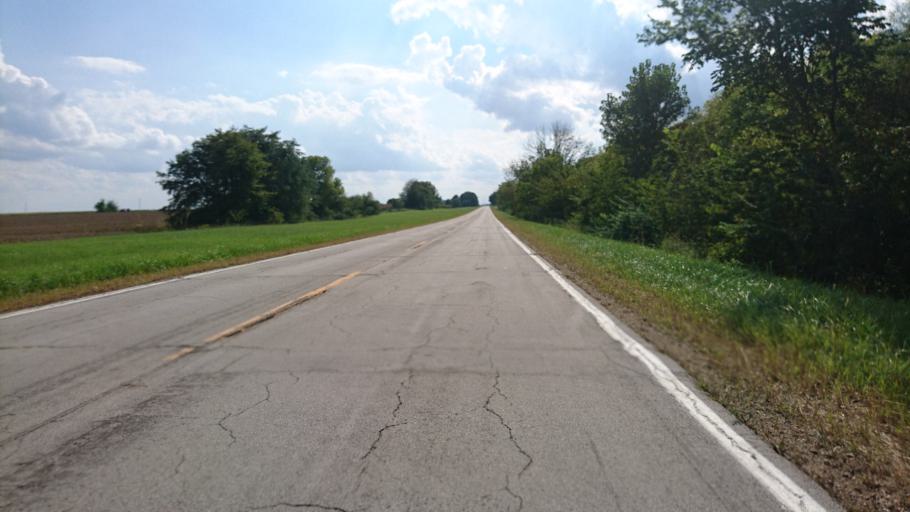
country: US
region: Illinois
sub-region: Logan County
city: Atlanta
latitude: 40.3503
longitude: -89.1275
